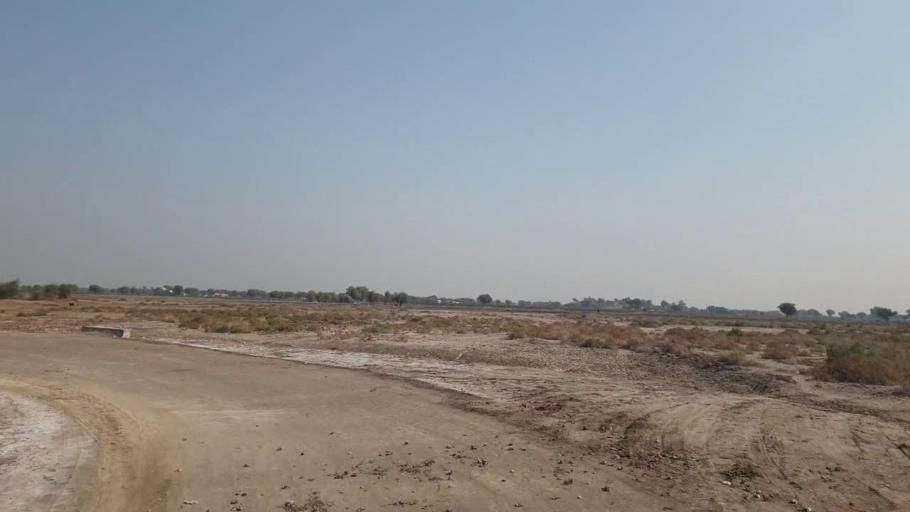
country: PK
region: Sindh
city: Sehwan
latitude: 26.4322
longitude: 67.7736
